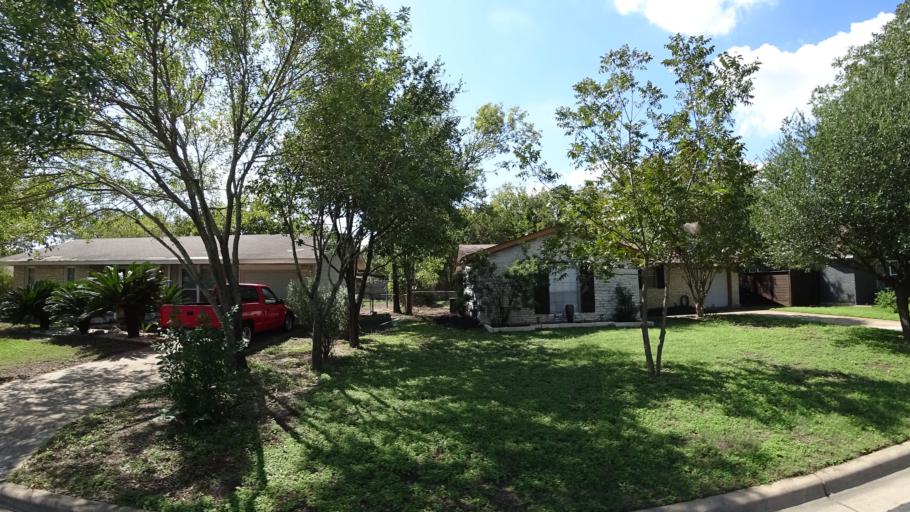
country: US
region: Texas
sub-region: Travis County
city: Austin
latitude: 30.3340
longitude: -97.7086
